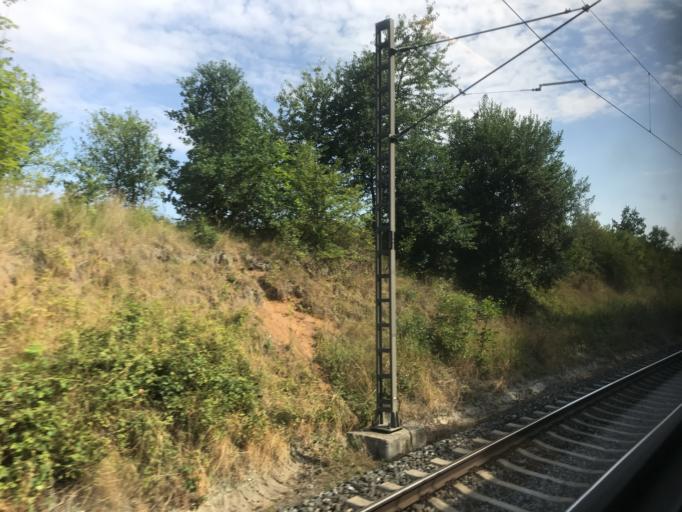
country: CZ
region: Central Bohemia
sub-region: Okres Benesov
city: Benesov
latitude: 49.7582
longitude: 14.6772
